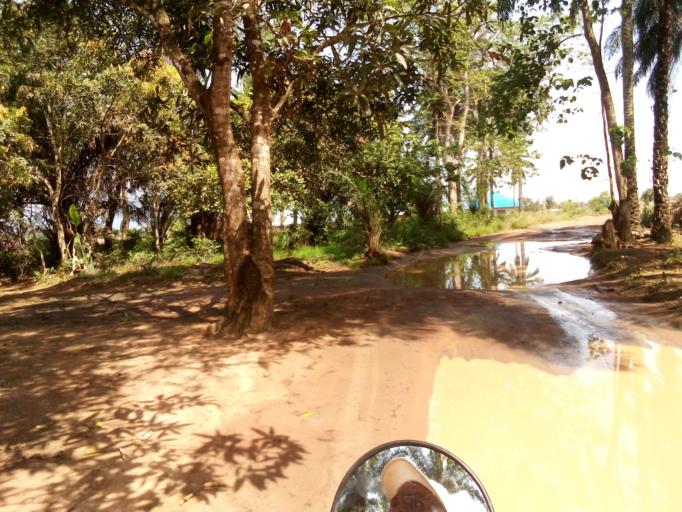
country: SL
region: Western Area
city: Waterloo
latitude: 8.3415
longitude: -13.0104
